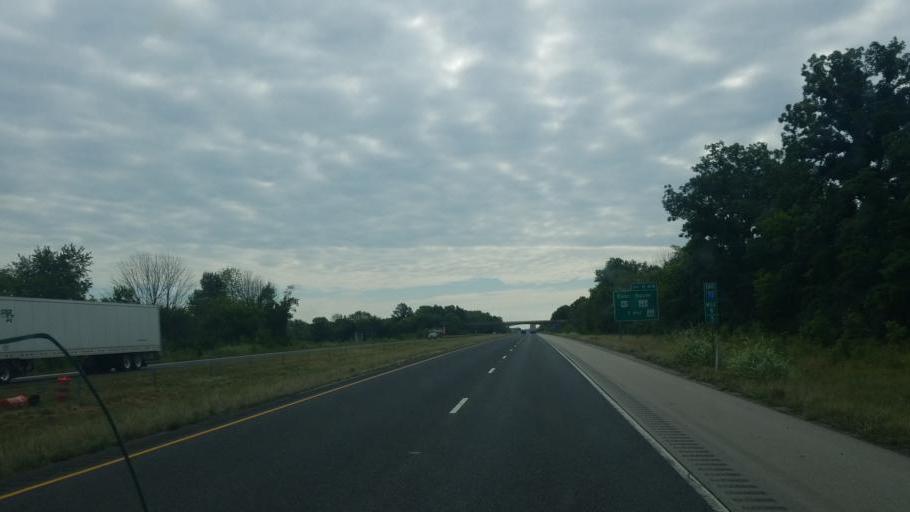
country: US
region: Indiana
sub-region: Vigo County
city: Terre Haute
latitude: 39.4307
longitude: -87.3651
